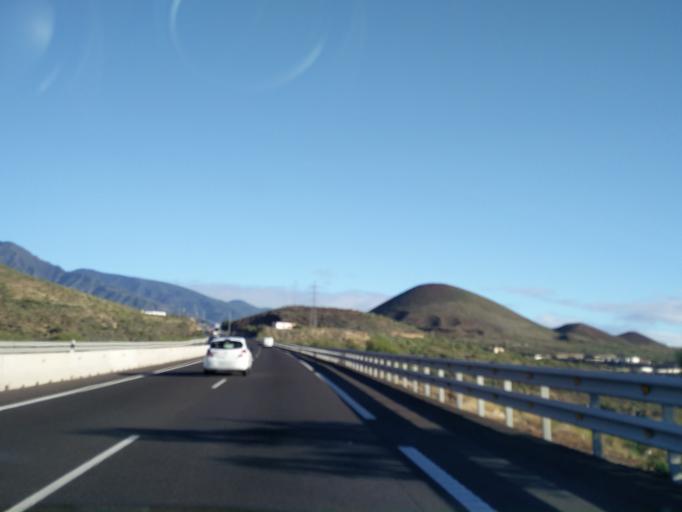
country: ES
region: Canary Islands
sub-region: Provincia de Santa Cruz de Tenerife
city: Guimar
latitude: 28.2959
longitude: -16.3829
